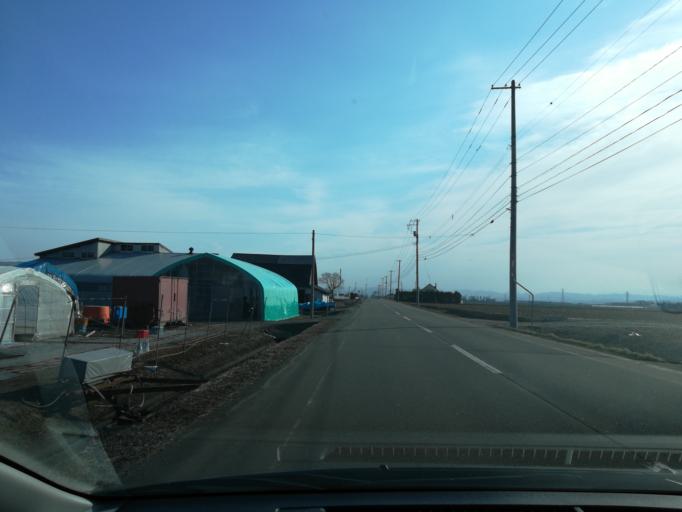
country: JP
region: Hokkaido
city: Iwamizawa
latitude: 43.1639
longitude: 141.6552
